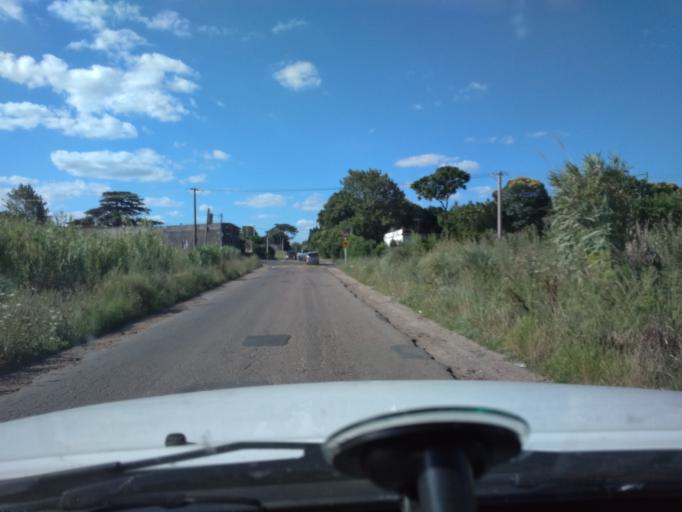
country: UY
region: Canelones
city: La Paz
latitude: -34.8044
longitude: -56.2098
